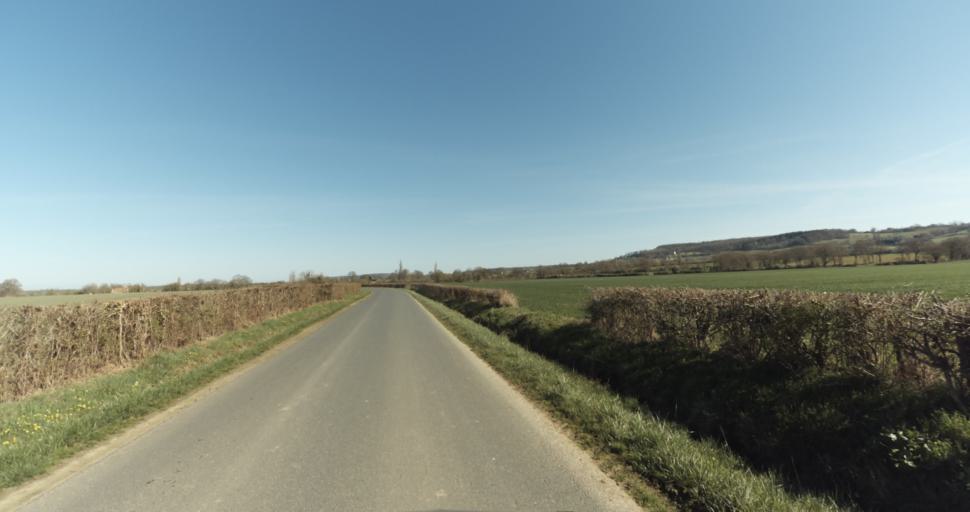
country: FR
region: Lower Normandy
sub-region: Departement de l'Orne
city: Trun
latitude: 48.9253
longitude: 0.0297
